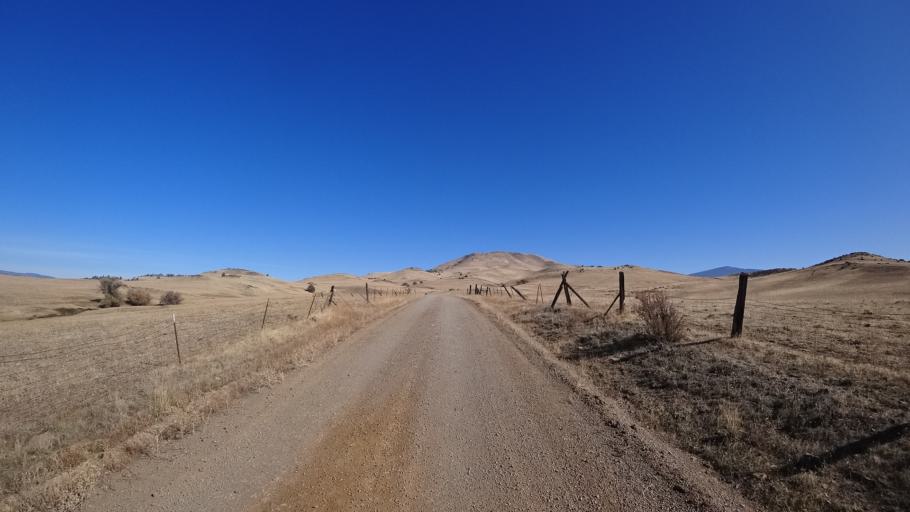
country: US
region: California
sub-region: Siskiyou County
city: Montague
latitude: 41.8458
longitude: -122.4407
